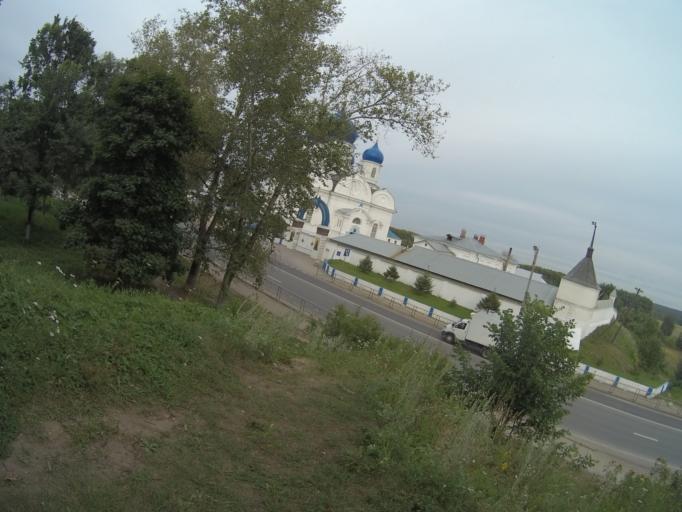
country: RU
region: Vladimir
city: Bogolyubovo
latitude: 56.1961
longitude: 40.5342
